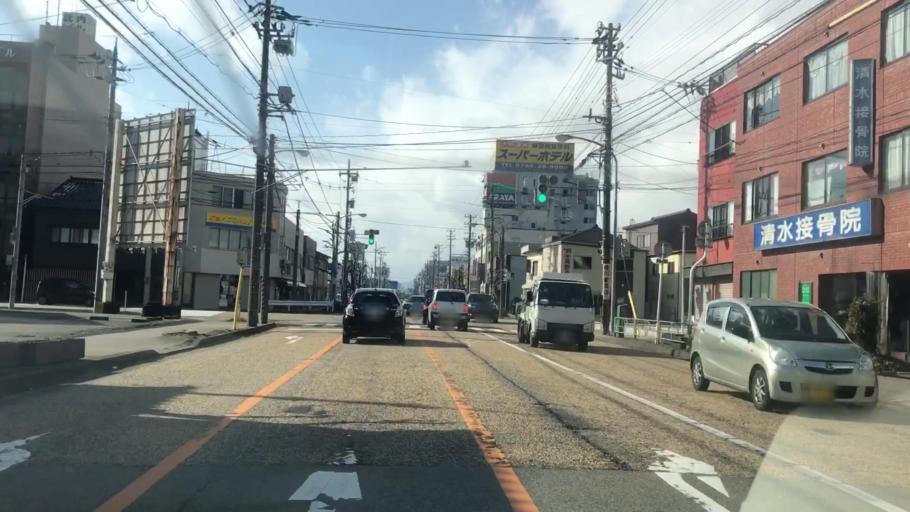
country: JP
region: Toyama
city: Takaoka
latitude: 36.7387
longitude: 137.0205
